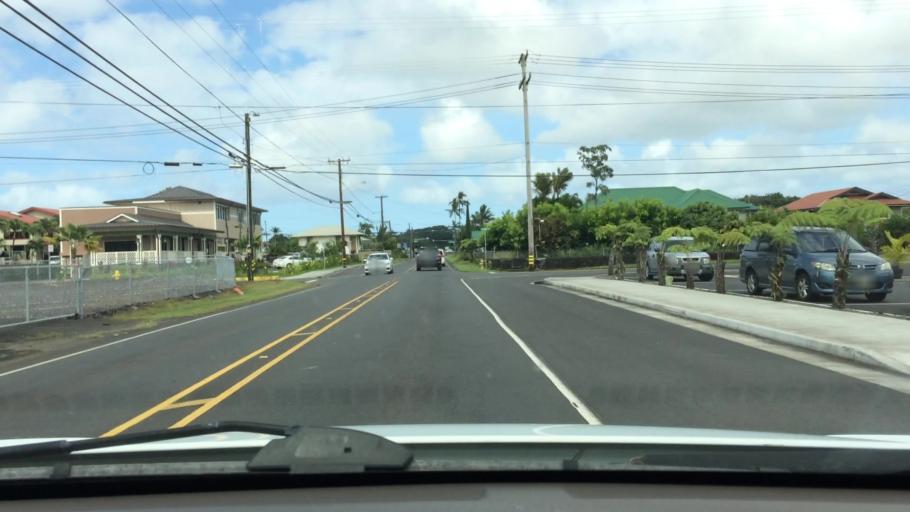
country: US
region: Hawaii
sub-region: Hawaii County
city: Hilo
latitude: 19.7117
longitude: -155.0677
